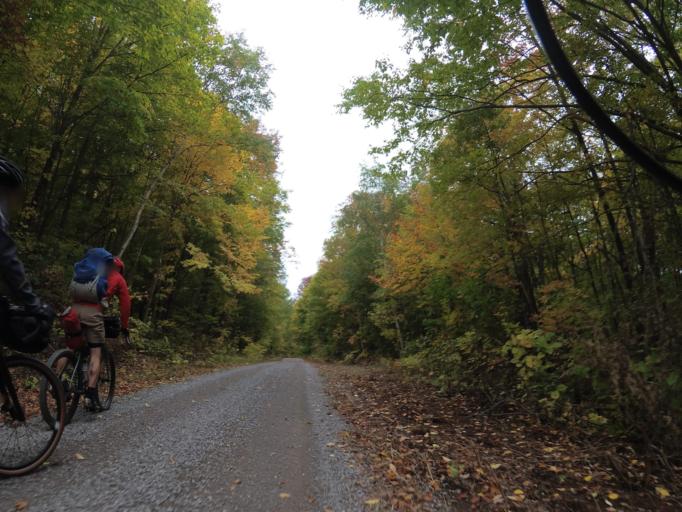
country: CA
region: Ontario
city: Pembroke
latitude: 45.3461
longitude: -77.1721
